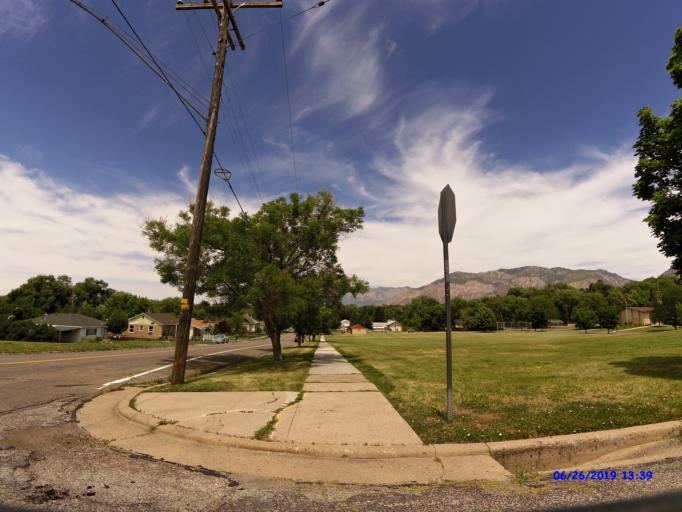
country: US
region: Utah
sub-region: Weber County
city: South Ogden
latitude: 41.2033
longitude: -111.9652
